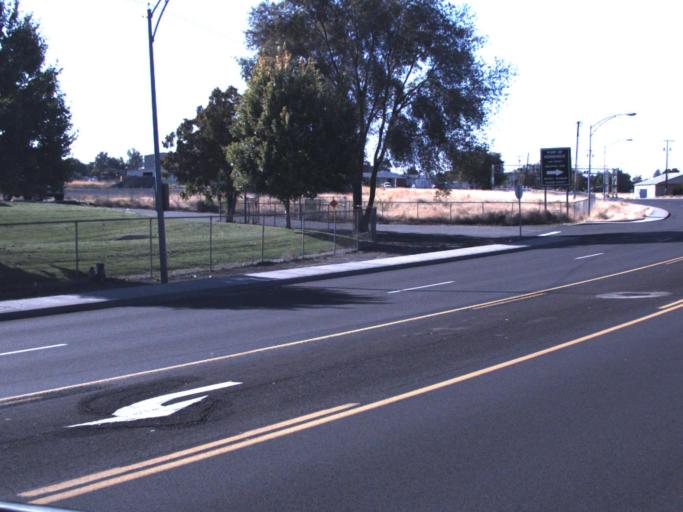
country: US
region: Washington
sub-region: Franklin County
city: Pasco
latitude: 46.2050
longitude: -119.1006
